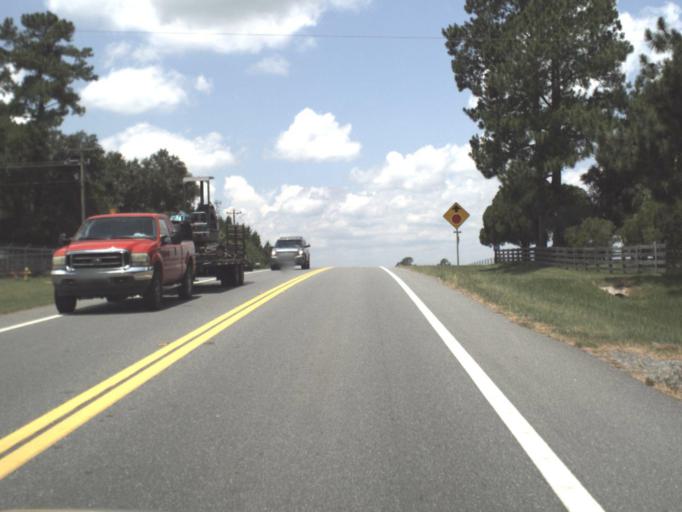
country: US
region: Florida
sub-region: Alachua County
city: High Springs
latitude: 30.0039
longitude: -82.5918
